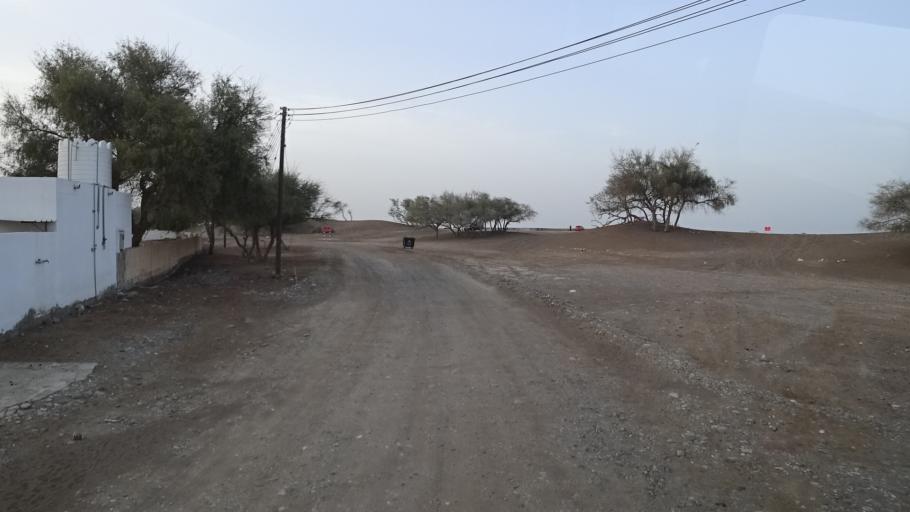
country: OM
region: Muhafazat Masqat
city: Muscat
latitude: 23.2173
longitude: 58.9745
